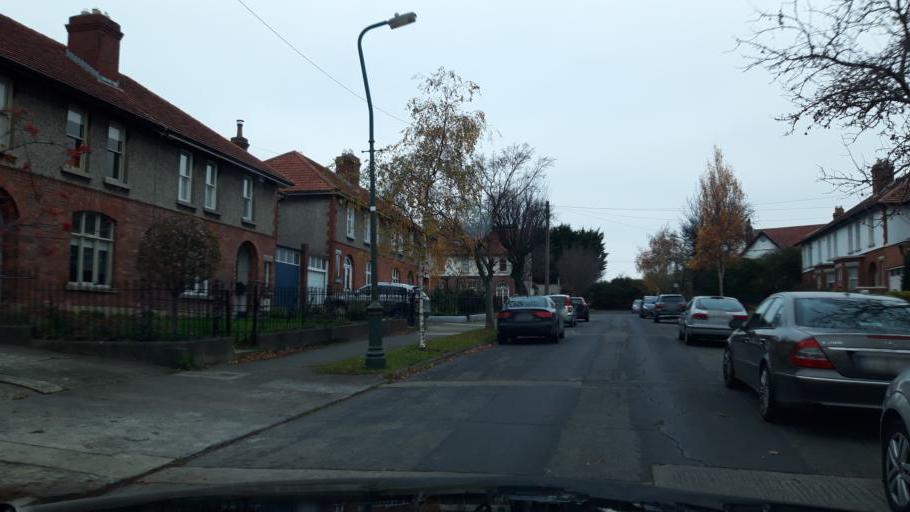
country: IE
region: Leinster
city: Glasnevin
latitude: 53.3773
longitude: -6.2724
